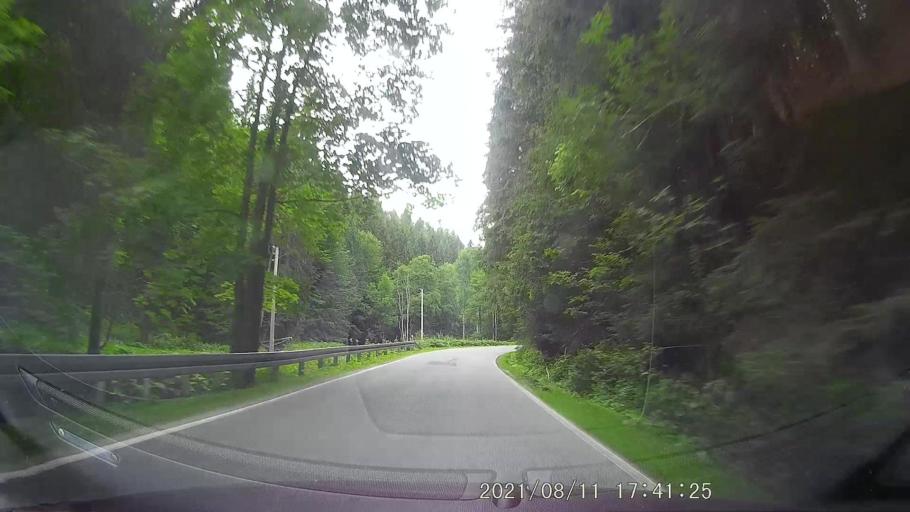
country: PL
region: Lower Silesian Voivodeship
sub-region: Powiat klodzki
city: Duszniki-Zdroj
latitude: 50.3667
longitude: 16.3915
